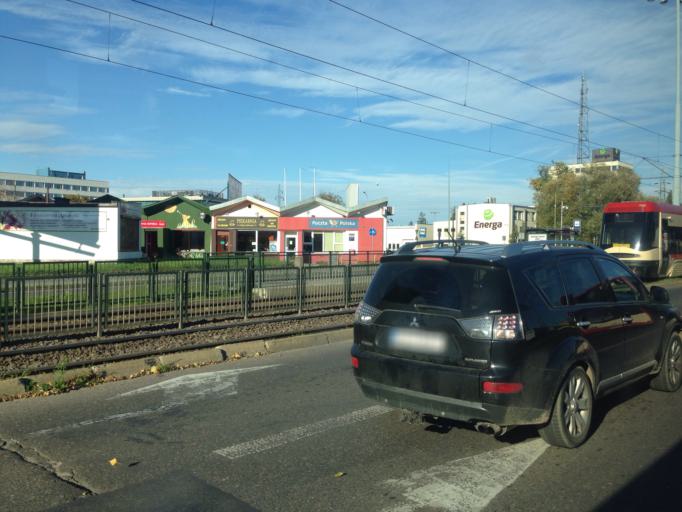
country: PL
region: Pomeranian Voivodeship
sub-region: Gdansk
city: Gdansk
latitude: 54.3786
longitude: 18.6331
